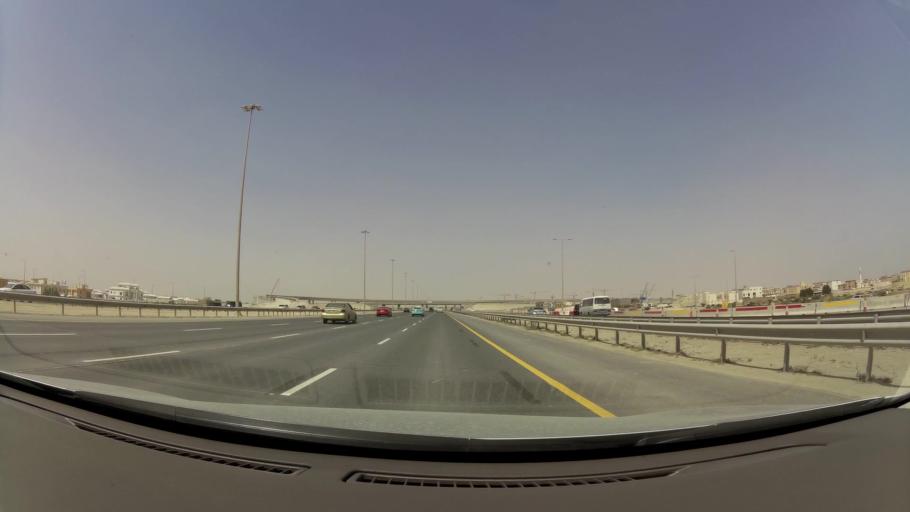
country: QA
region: Baladiyat Umm Salal
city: Umm Salal Muhammad
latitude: 25.3965
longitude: 51.4321
